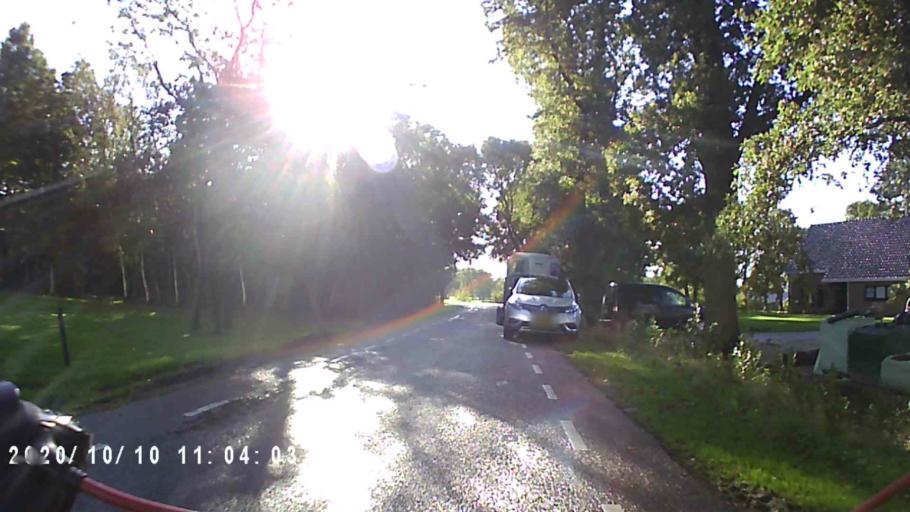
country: NL
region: Friesland
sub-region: Gemeente Achtkarspelen
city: Surhuisterveen
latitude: 53.1325
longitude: 6.2244
